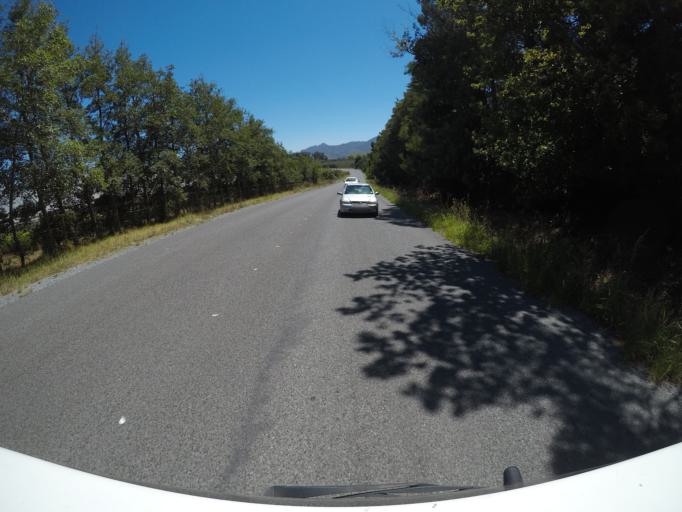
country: ZA
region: Western Cape
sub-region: Overberg District Municipality
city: Grabouw
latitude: -34.1711
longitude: 19.0349
